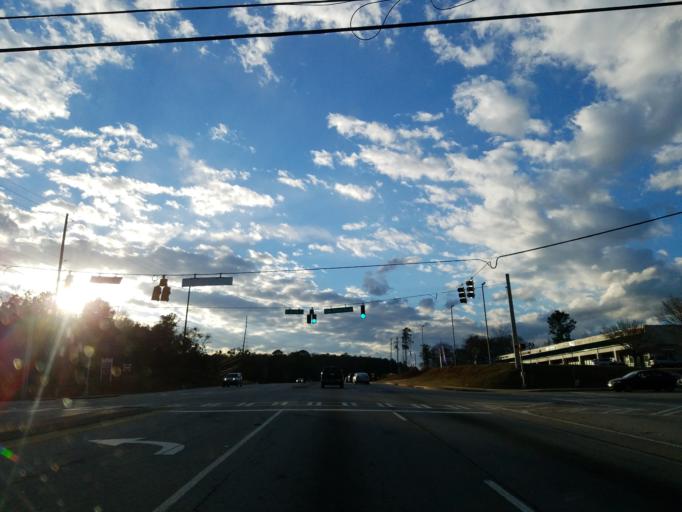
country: US
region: Georgia
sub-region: Henry County
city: McDonough
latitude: 33.4595
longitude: -84.1922
